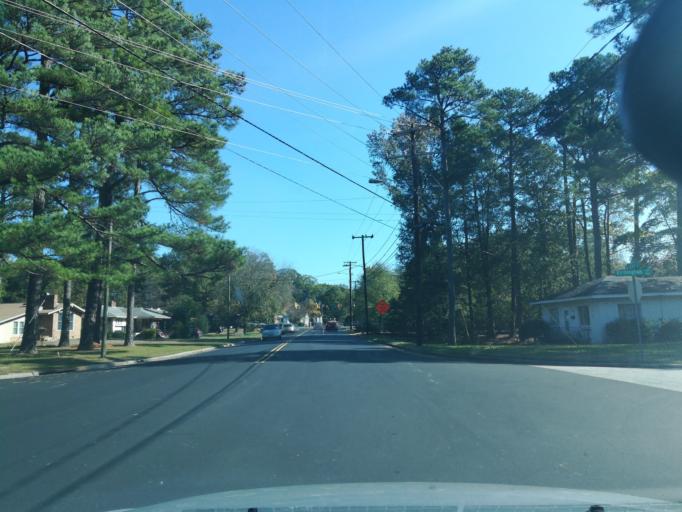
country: US
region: North Carolina
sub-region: Durham County
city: Durham
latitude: 36.0402
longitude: -78.9074
